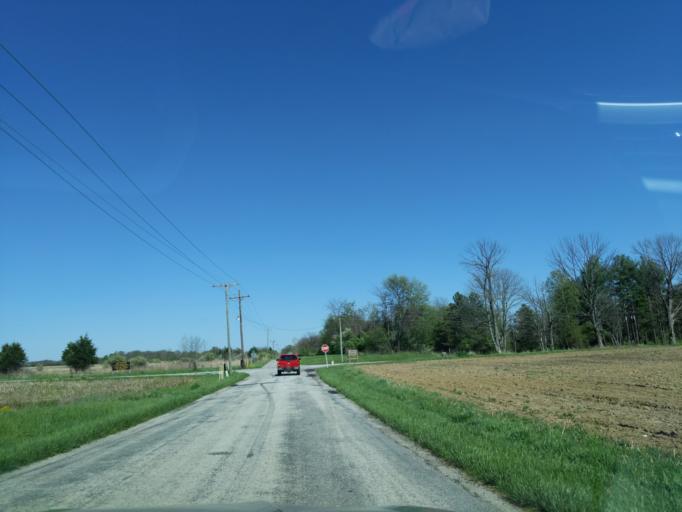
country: US
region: Indiana
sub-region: Decatur County
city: Greensburg
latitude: 39.2928
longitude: -85.4707
